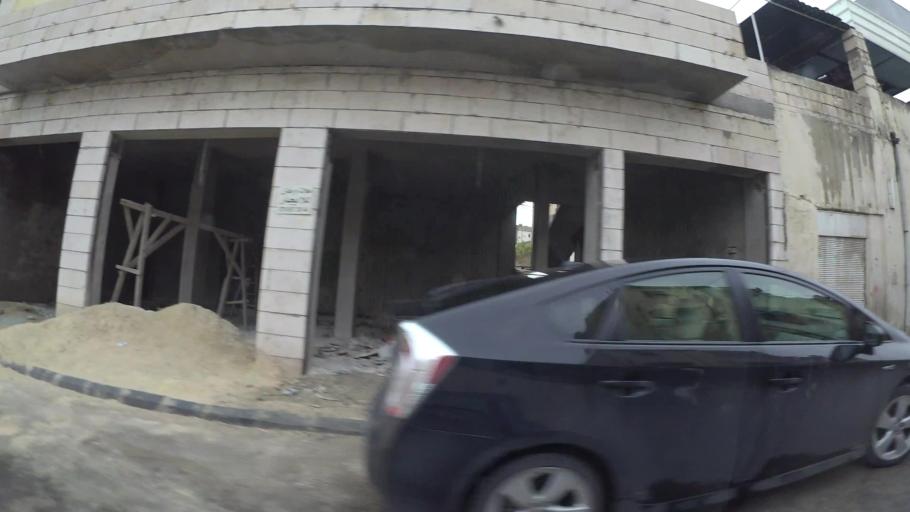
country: JO
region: Amman
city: Amman
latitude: 31.9545
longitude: 35.9414
